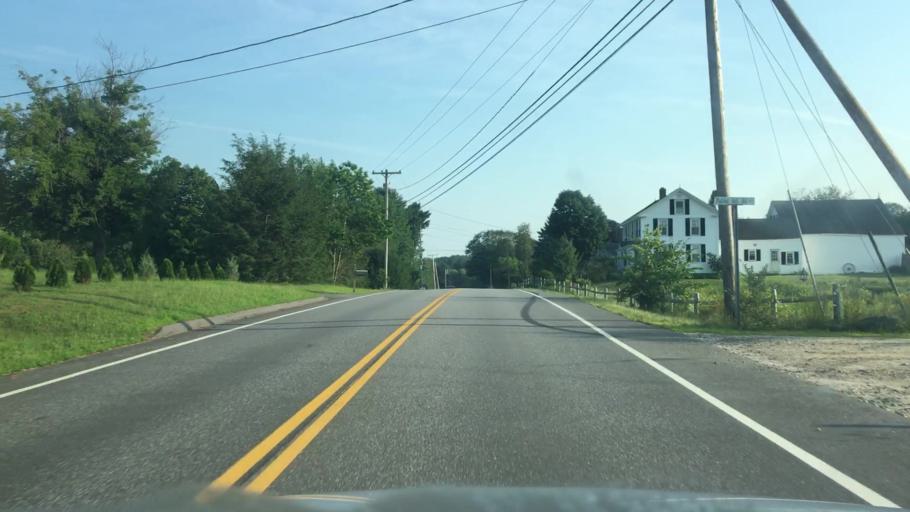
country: US
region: Maine
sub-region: Cumberland County
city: Freeport
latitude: 43.8986
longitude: -70.0941
